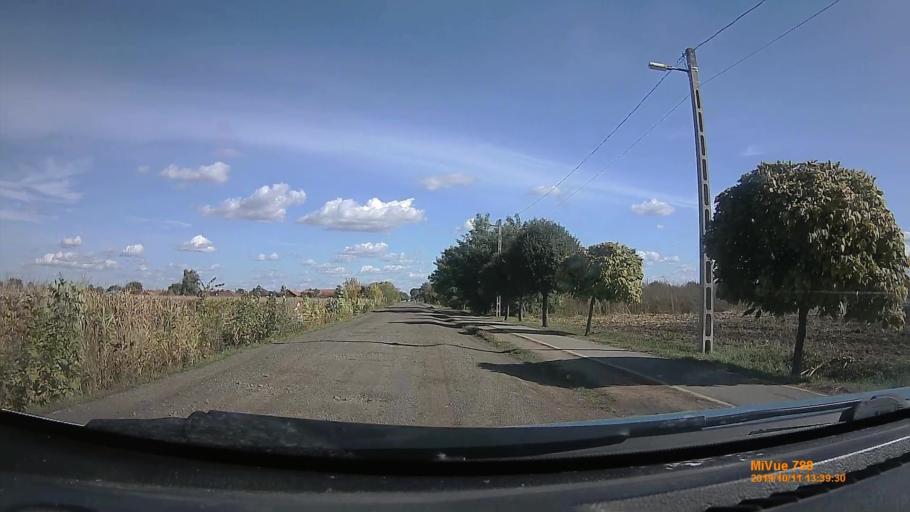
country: HU
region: Hajdu-Bihar
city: Balmazujvaros
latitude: 47.5399
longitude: 21.3316
